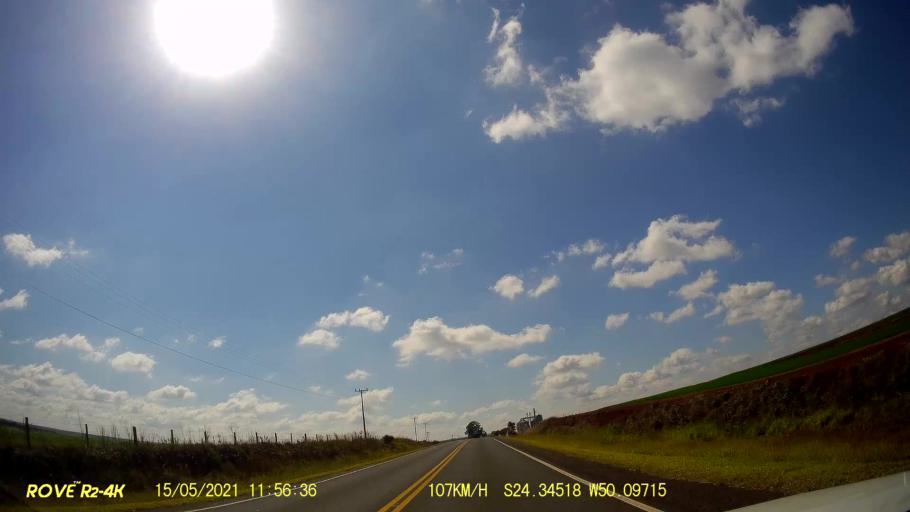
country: BR
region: Parana
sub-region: Pirai Do Sul
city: Pirai do Sul
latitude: -24.3454
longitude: -50.0973
